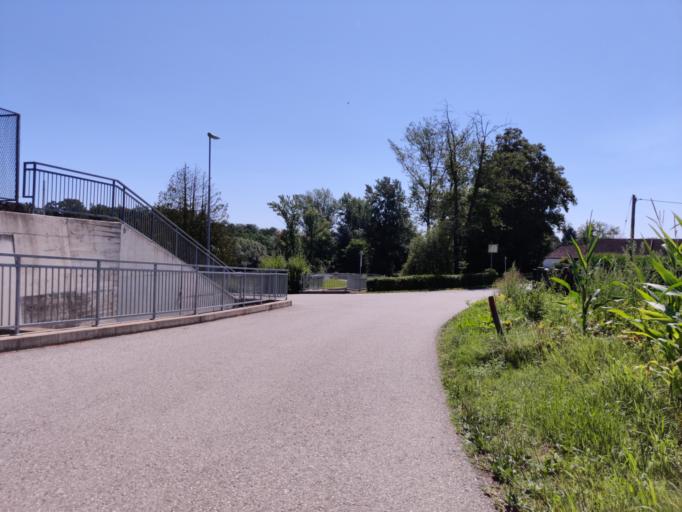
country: AT
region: Styria
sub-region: Politischer Bezirk Leibnitz
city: Ragnitz
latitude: 46.8279
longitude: 15.5655
